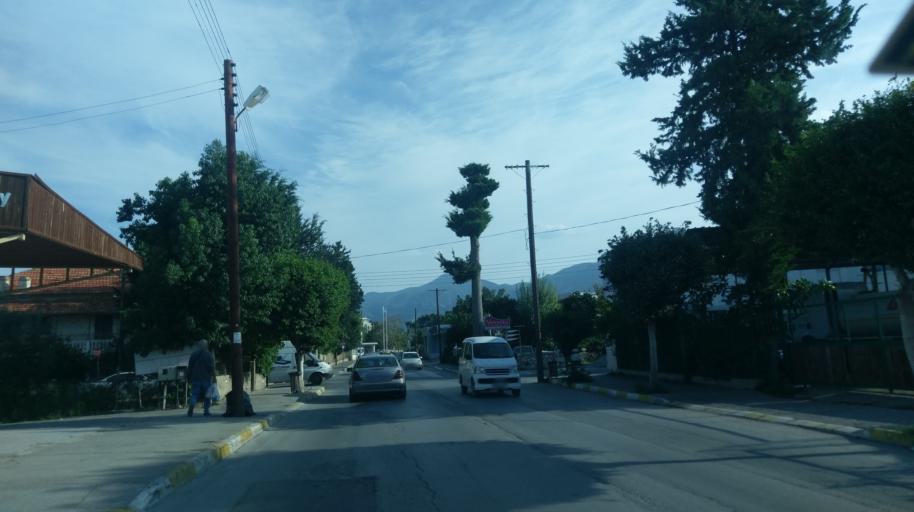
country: CY
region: Keryneia
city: Kyrenia
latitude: 35.3383
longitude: 33.3241
